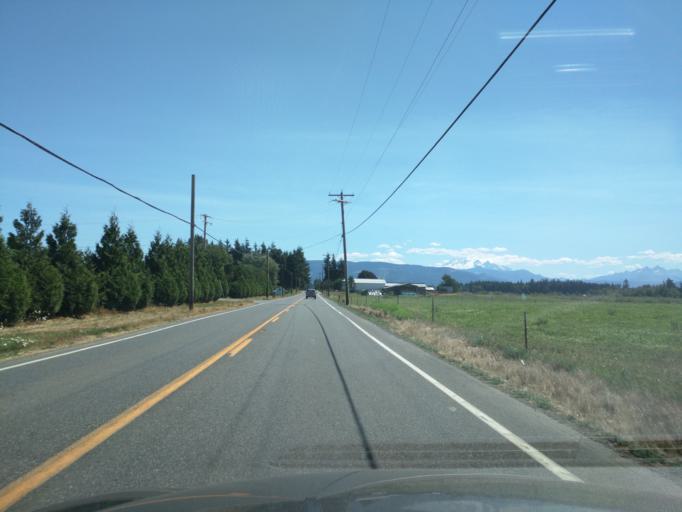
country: US
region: Washington
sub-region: Whatcom County
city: Lynden
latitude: 48.8917
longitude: -122.4284
